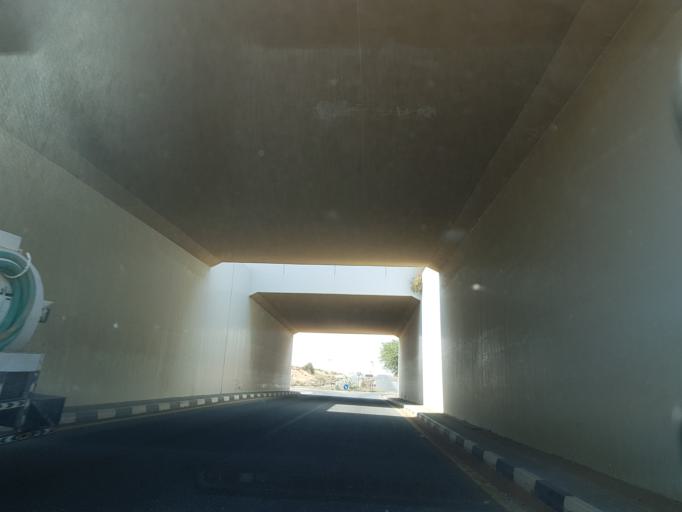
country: AE
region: Ra's al Khaymah
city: Ras al-Khaimah
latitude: 25.6995
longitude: 55.8741
